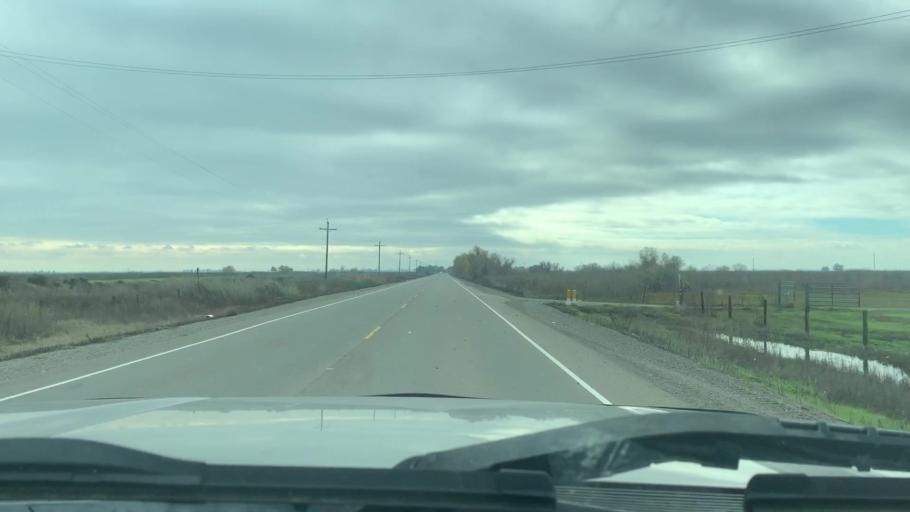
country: US
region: California
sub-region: Merced County
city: Los Banos
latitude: 37.1427
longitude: -120.8276
